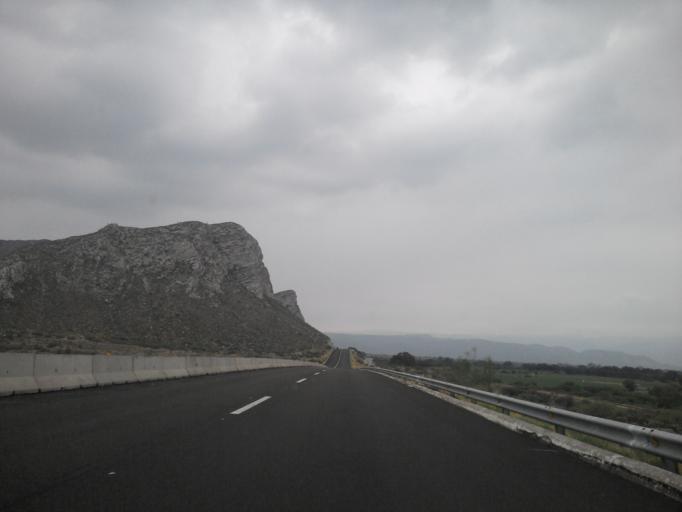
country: MX
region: Durango
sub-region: Lerdo
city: La Goma
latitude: 25.4827
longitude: -103.6443
